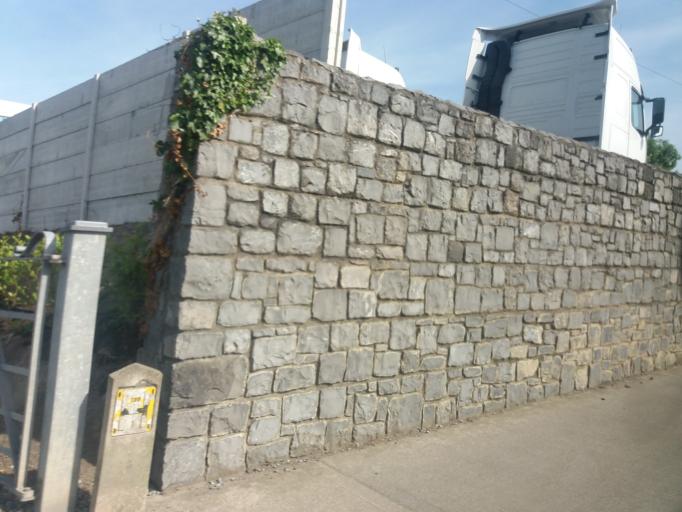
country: IE
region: Leinster
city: Lusk
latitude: 53.5248
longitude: -6.1657
